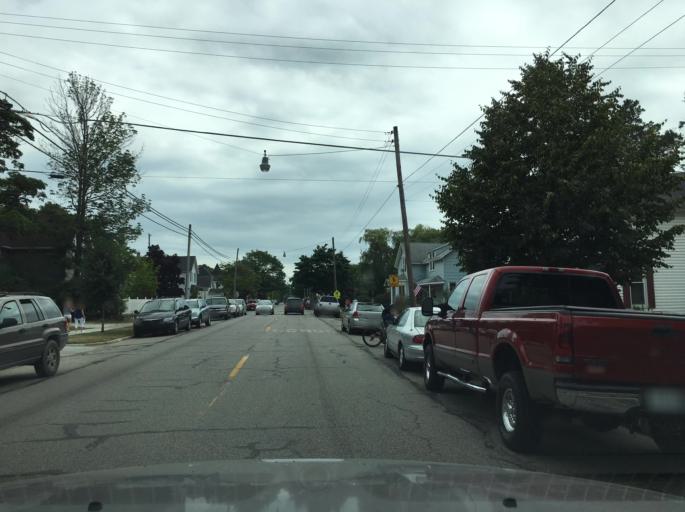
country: US
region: Michigan
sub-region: Mason County
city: Ludington
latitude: 43.9543
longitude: -86.4394
